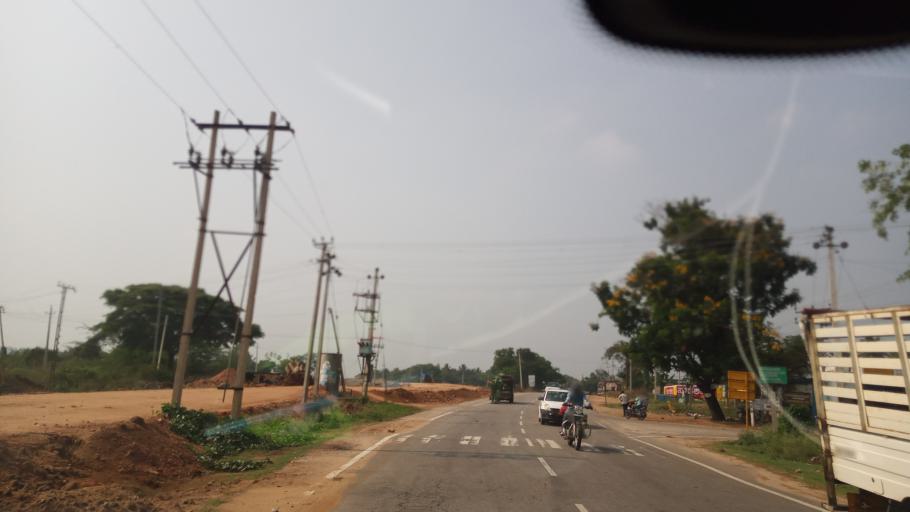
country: IN
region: Karnataka
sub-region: Mandya
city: Pandavapura
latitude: 12.5257
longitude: 76.6720
